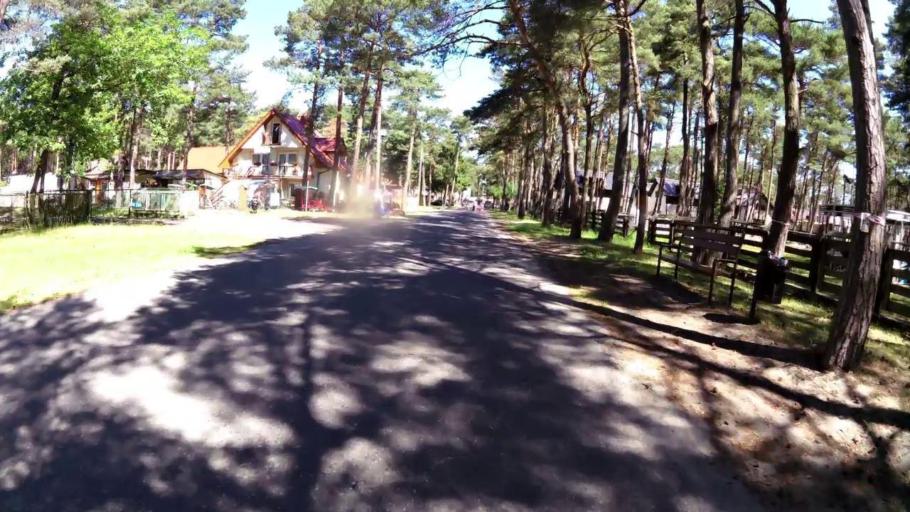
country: PL
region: West Pomeranian Voivodeship
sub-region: Powiat gryficki
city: Pobierowo
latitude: 54.0559
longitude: 14.9190
